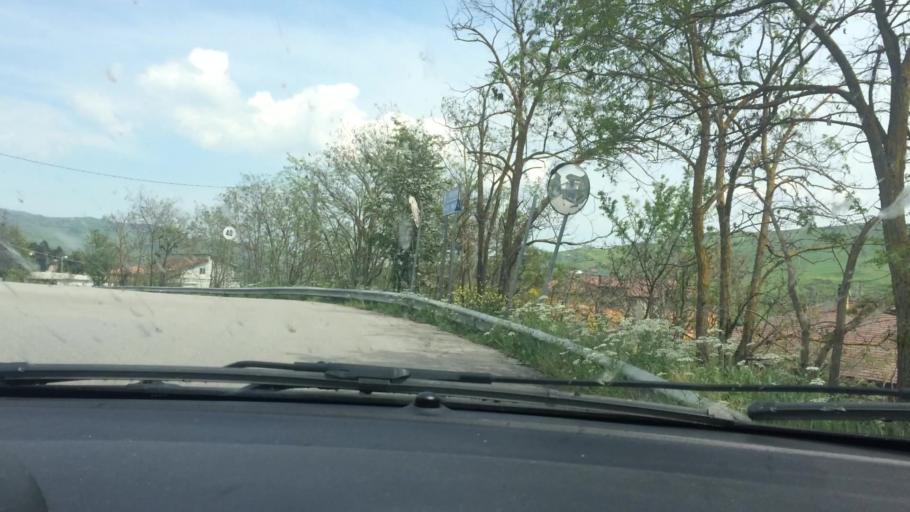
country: IT
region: Basilicate
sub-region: Provincia di Potenza
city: Potenza
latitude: 40.6436
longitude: 15.8523
